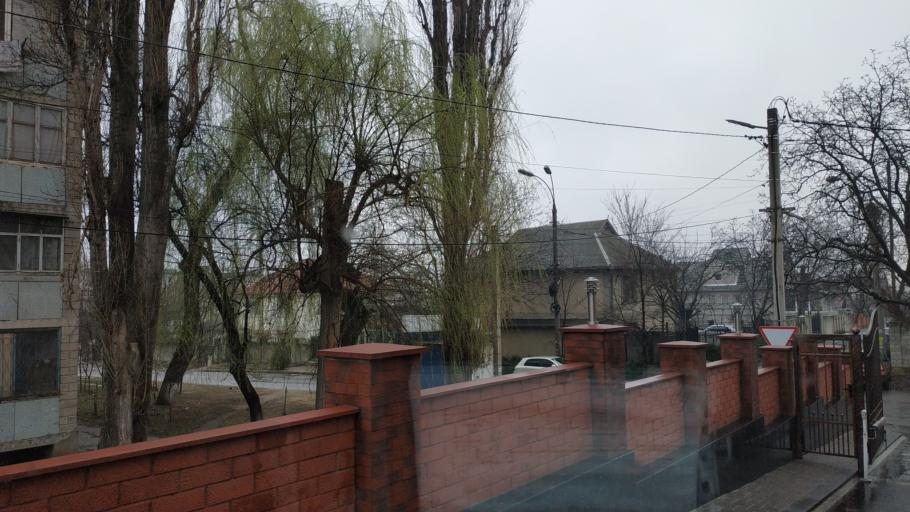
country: MD
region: Chisinau
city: Vatra
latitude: 47.0347
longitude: 28.7832
